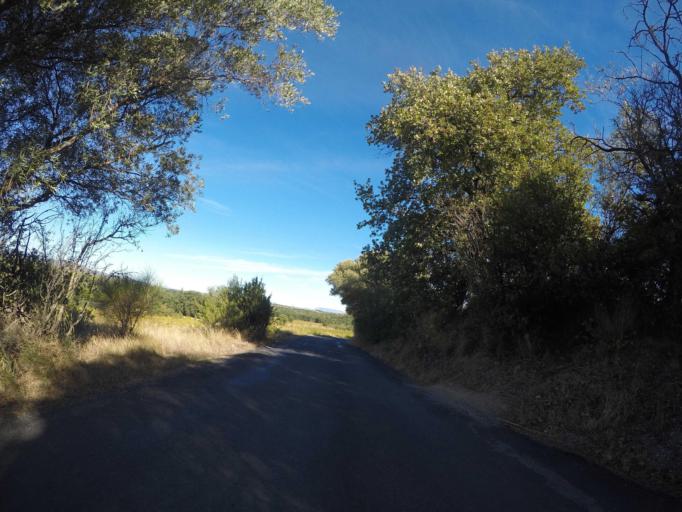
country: FR
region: Languedoc-Roussillon
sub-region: Departement des Pyrenees-Orientales
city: Trouillas
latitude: 42.5826
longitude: 2.8101
